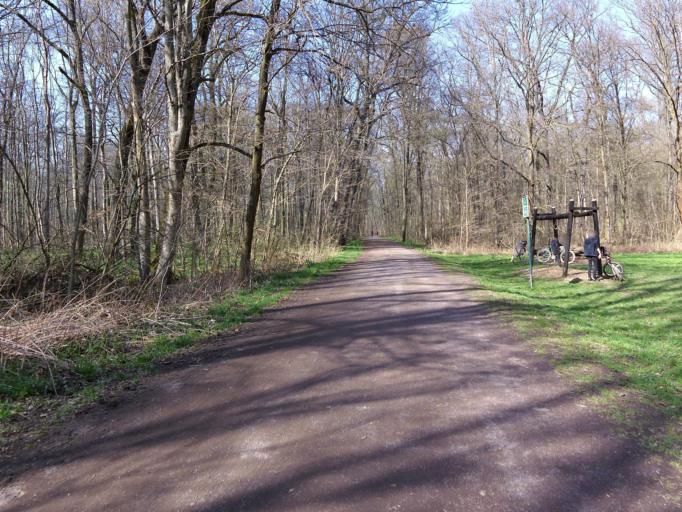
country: DE
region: Saxony
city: Leipzig
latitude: 51.3641
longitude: 12.2964
